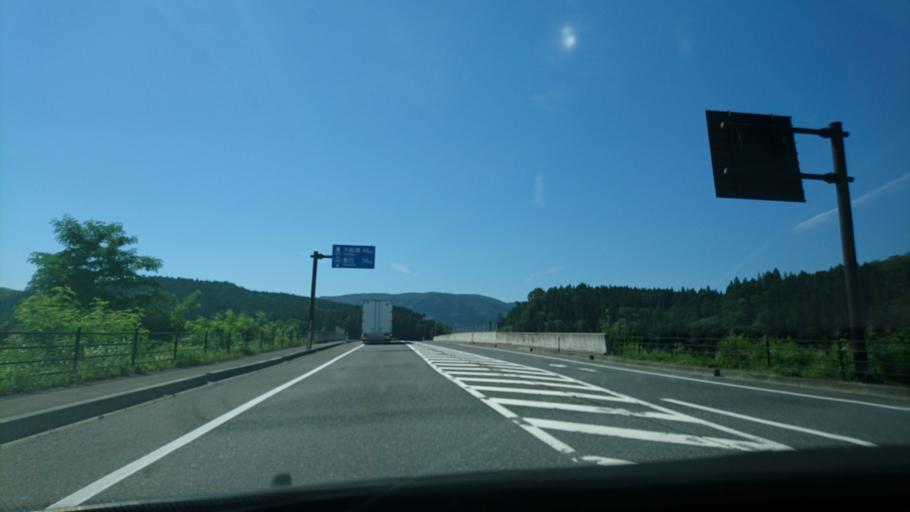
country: JP
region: Iwate
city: Tono
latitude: 39.2916
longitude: 141.5785
